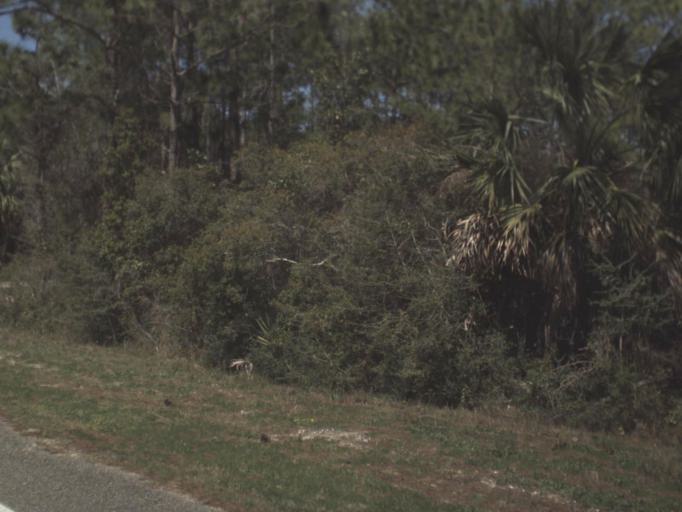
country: US
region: Florida
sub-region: Gulf County
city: Port Saint Joe
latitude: 29.7765
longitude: -85.2731
